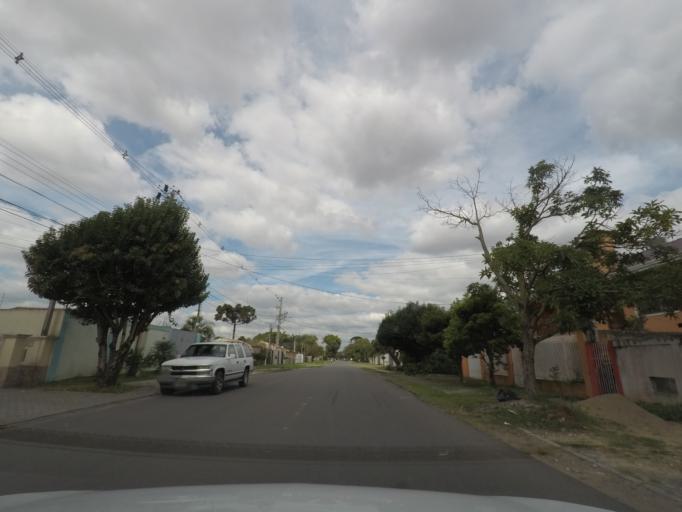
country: BR
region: Parana
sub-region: Sao Jose Dos Pinhais
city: Sao Jose dos Pinhais
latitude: -25.4845
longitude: -49.2432
